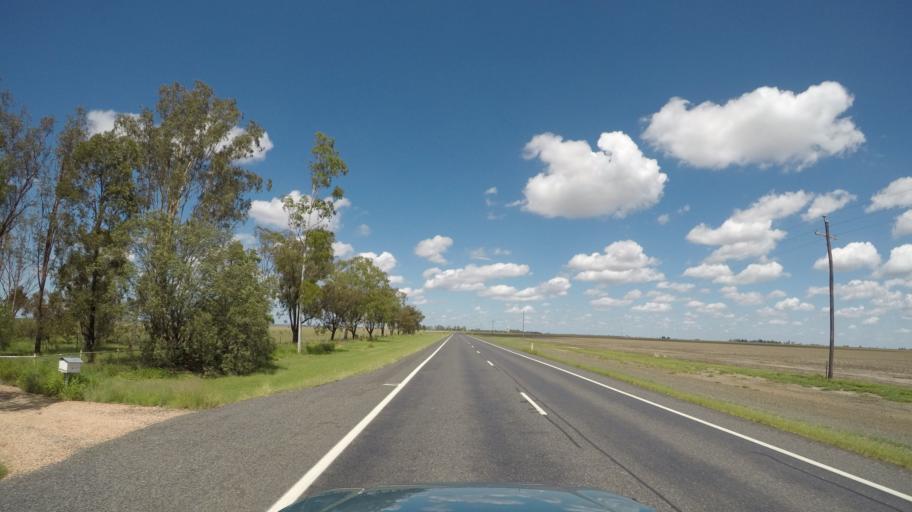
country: AU
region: Queensland
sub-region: Toowoomba
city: Oakey
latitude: -27.7580
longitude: 151.4861
